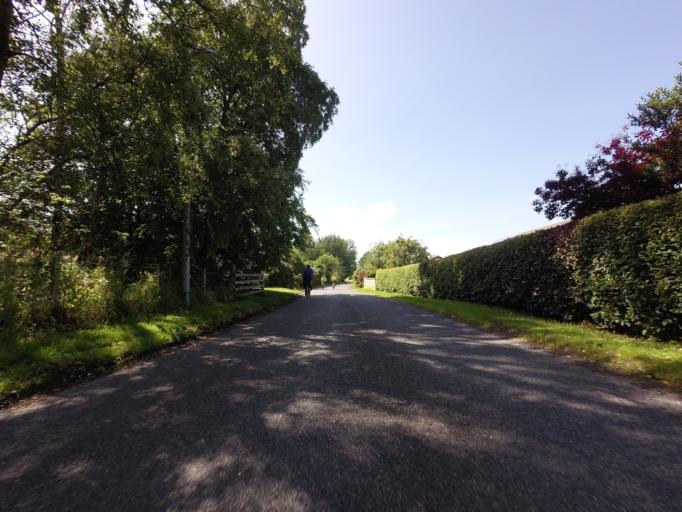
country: GB
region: Scotland
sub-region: Highland
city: Inverness
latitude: 57.4733
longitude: -4.1665
